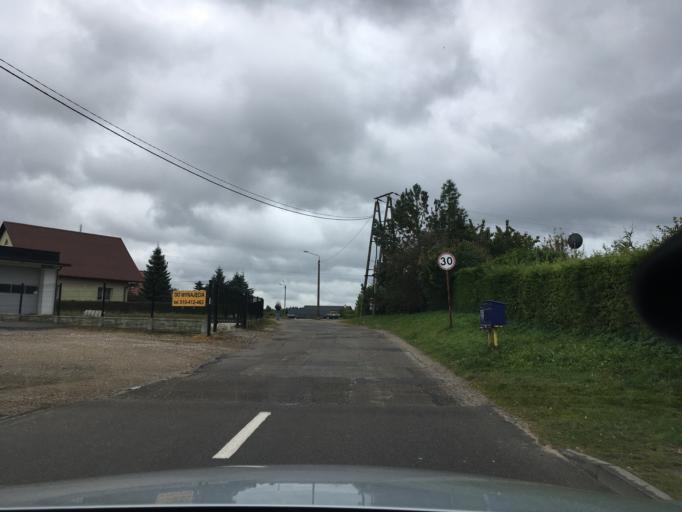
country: PL
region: Pomeranian Voivodeship
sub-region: Powiat koscierski
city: Koscierzyna
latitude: 54.1148
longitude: 17.9919
